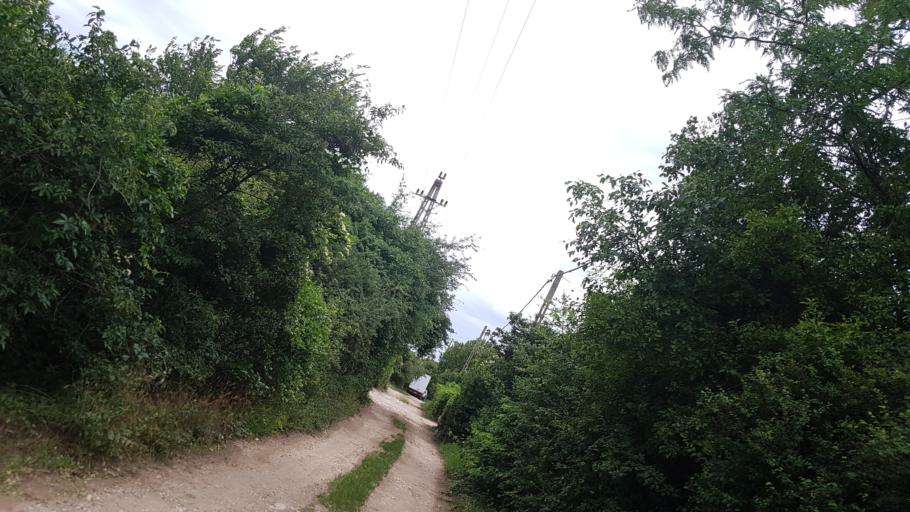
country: HU
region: Pest
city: Urom
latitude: 47.6088
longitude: 19.0300
